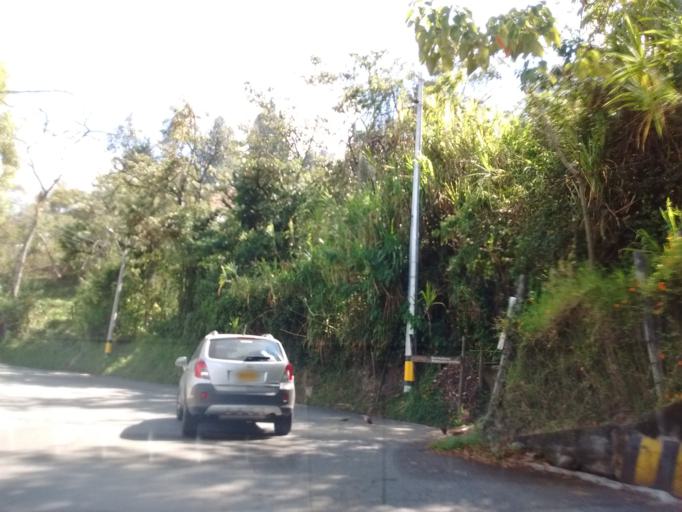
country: CO
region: Antioquia
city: Medellin
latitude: 6.2375
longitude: -75.5173
